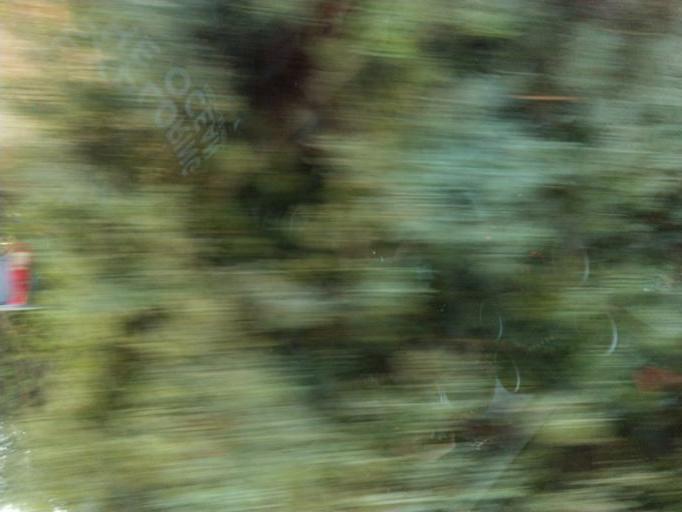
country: ES
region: Balearic Islands
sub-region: Illes Balears
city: Ses Salines
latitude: 39.3348
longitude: 3.0322
